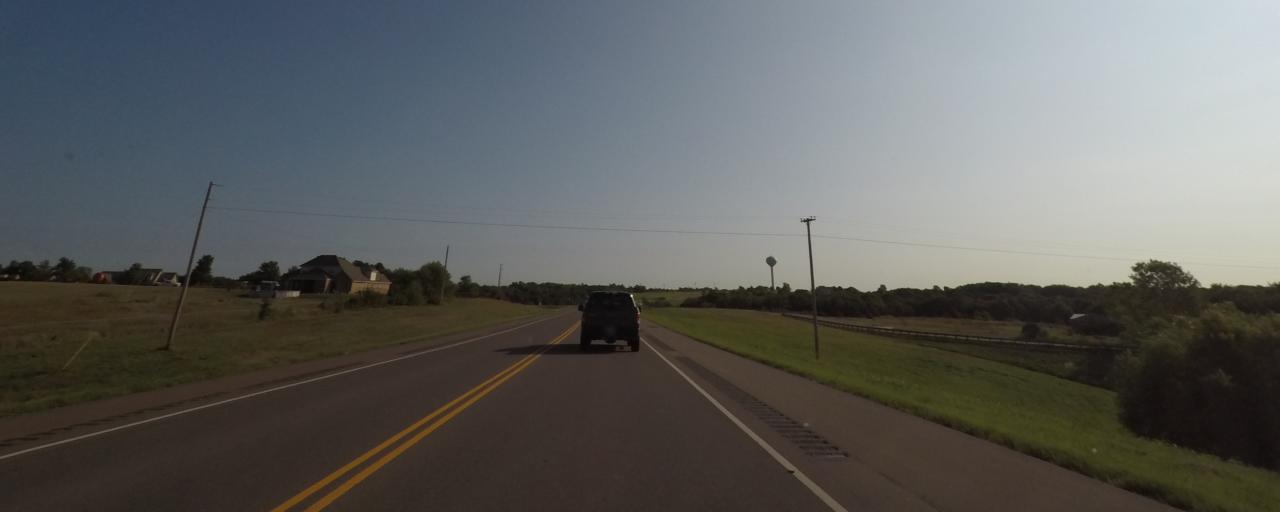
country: US
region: Oklahoma
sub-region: McClain County
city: Blanchard
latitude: 35.1180
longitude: -97.7072
